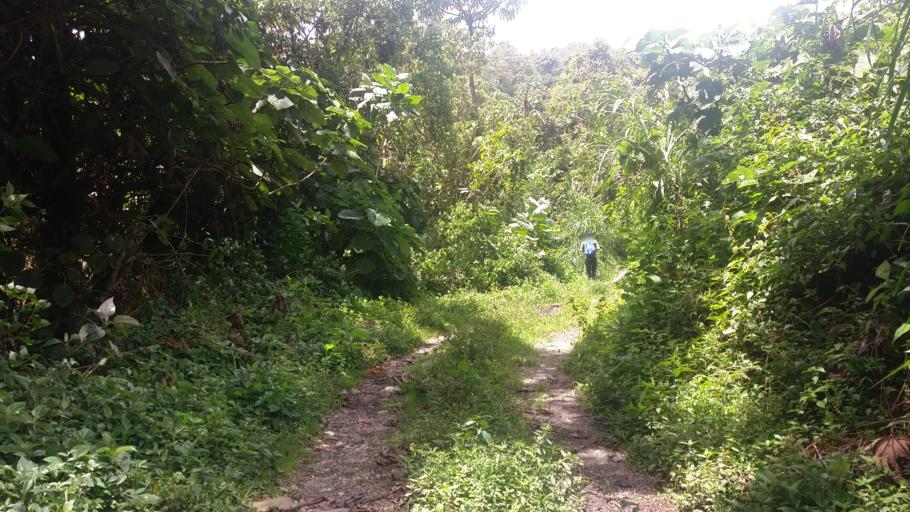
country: BO
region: Cochabamba
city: Colomi
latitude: -17.0853
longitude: -66.0106
